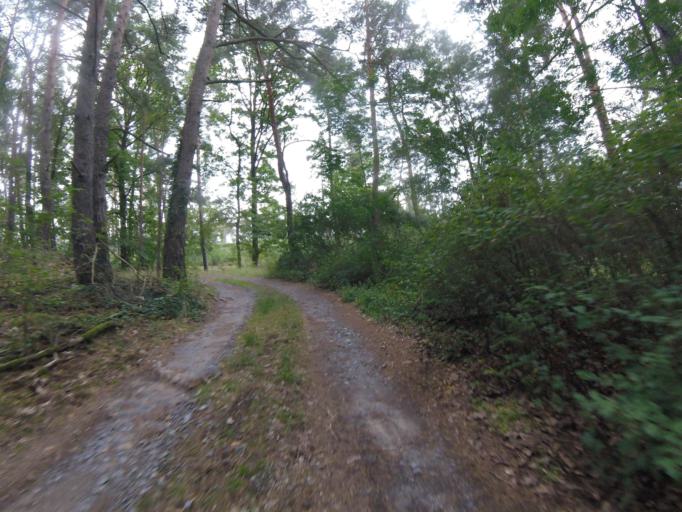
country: DE
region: Brandenburg
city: Bestensee
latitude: 52.2188
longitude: 13.6502
